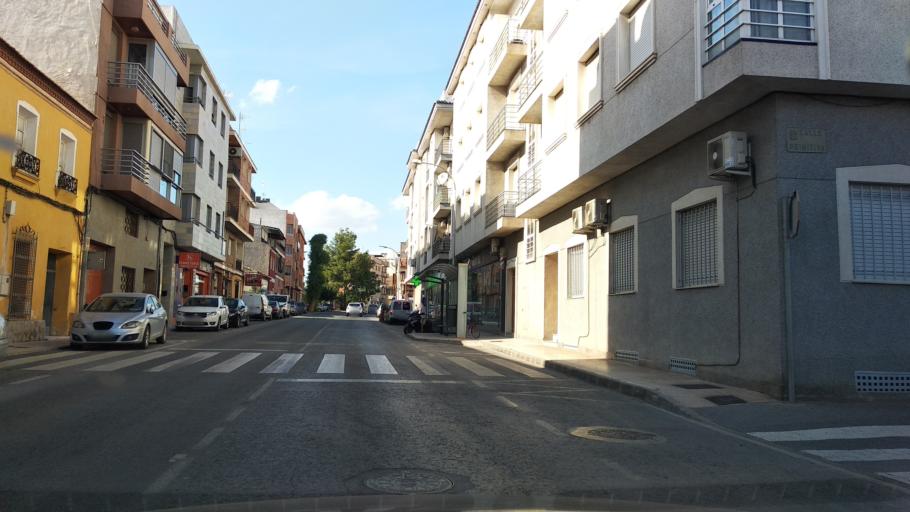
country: ES
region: Murcia
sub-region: Murcia
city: Santomera
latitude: 38.0610
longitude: -1.0529
